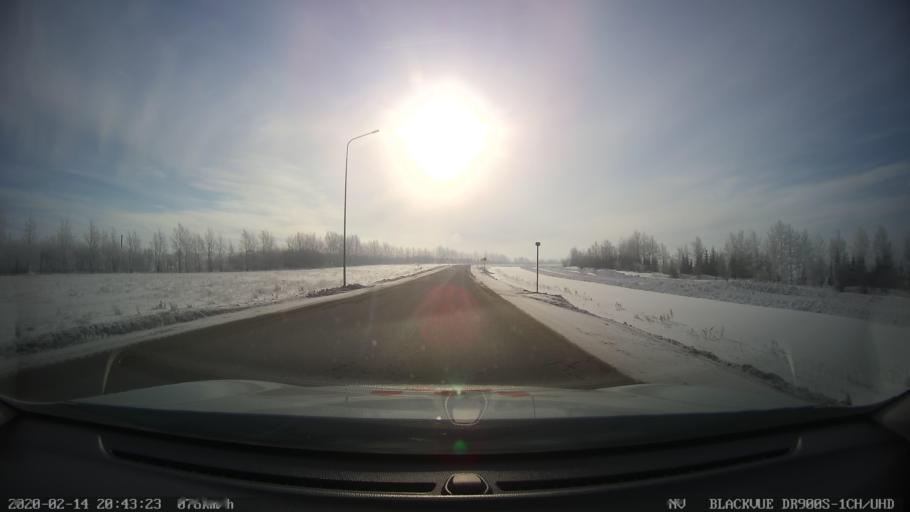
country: RU
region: Tatarstan
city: Kuybyshevskiy Zaton
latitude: 55.3087
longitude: 49.1475
